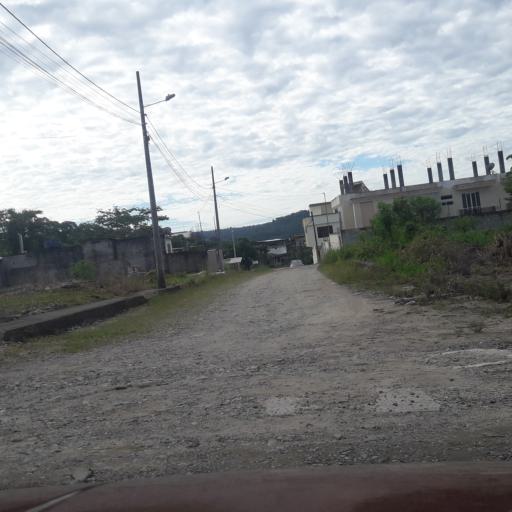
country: EC
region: Napo
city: Tena
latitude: -0.9828
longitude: -77.8249
